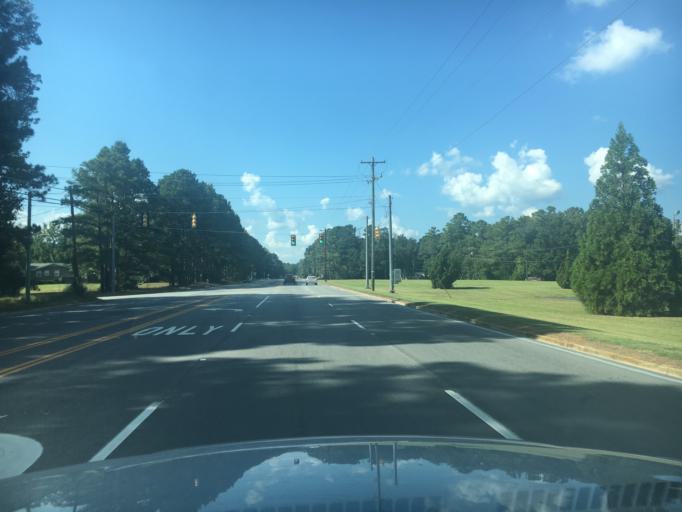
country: US
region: South Carolina
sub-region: Greenwood County
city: Greenwood
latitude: 34.2233
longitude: -82.1727
